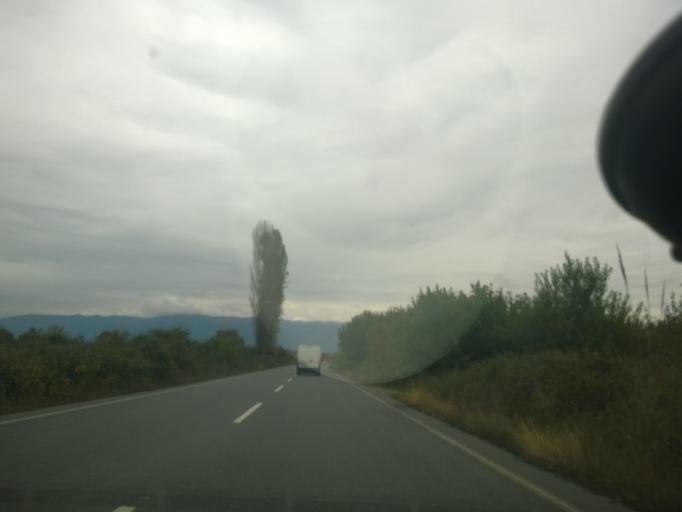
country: GR
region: Central Macedonia
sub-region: Nomos Pellis
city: Loutraki
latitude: 40.9724
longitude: 21.9716
